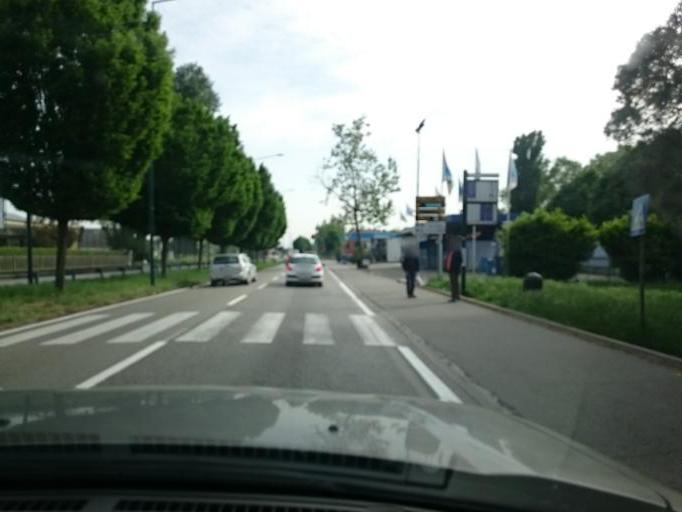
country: IT
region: Veneto
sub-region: Provincia di Venezia
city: Mestre
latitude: 45.4727
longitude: 12.2297
